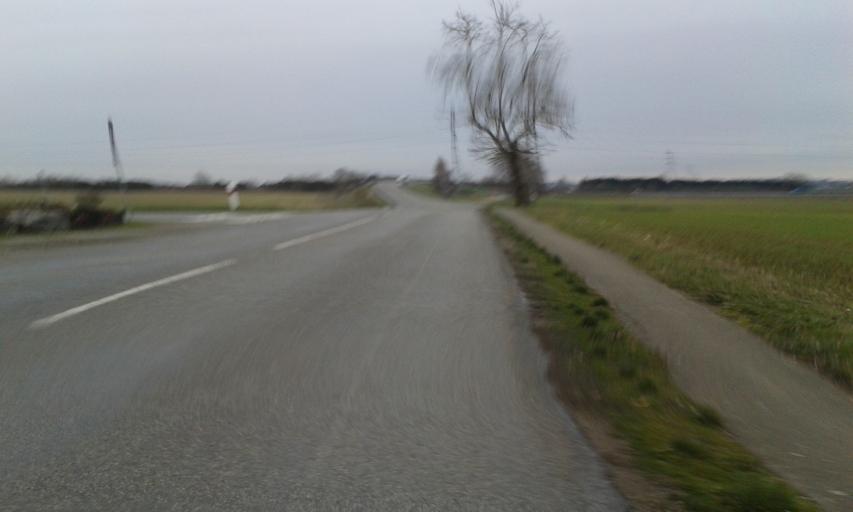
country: FR
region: Centre
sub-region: Departement du Loiret
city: Beaugency
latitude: 47.7941
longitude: 1.6030
